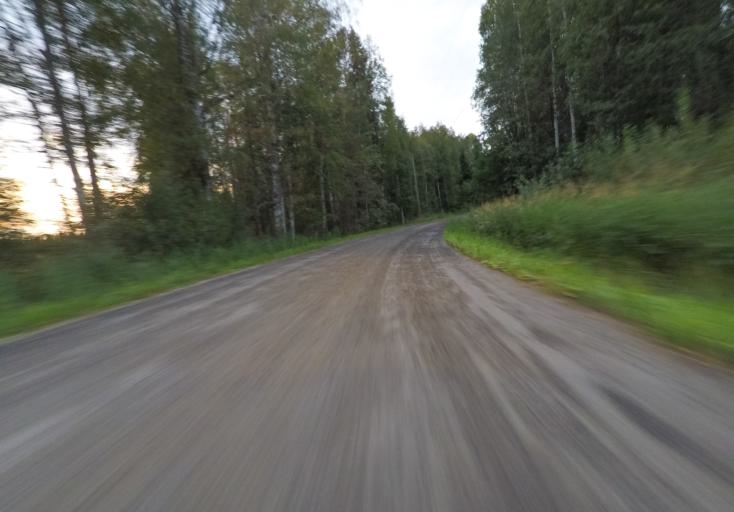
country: FI
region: Central Finland
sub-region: Jyvaeskylae
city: Hankasalmi
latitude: 62.4267
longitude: 26.6443
